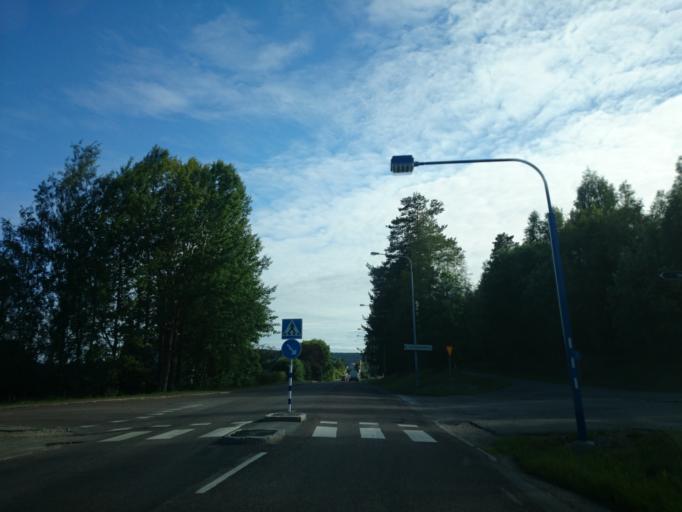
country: SE
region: Vaesternorrland
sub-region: Sundsvalls Kommun
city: Sundsvall
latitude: 62.4053
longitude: 17.3312
